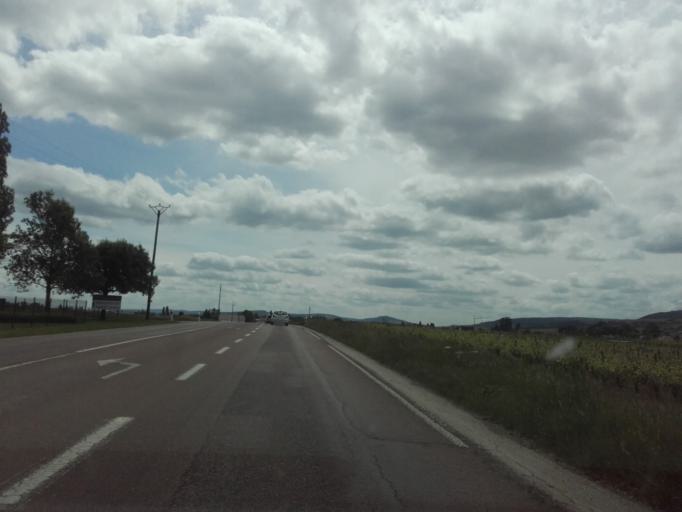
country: FR
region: Bourgogne
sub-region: Departement de la Cote-d'Or
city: Meursault
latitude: 46.9810
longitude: 4.7890
